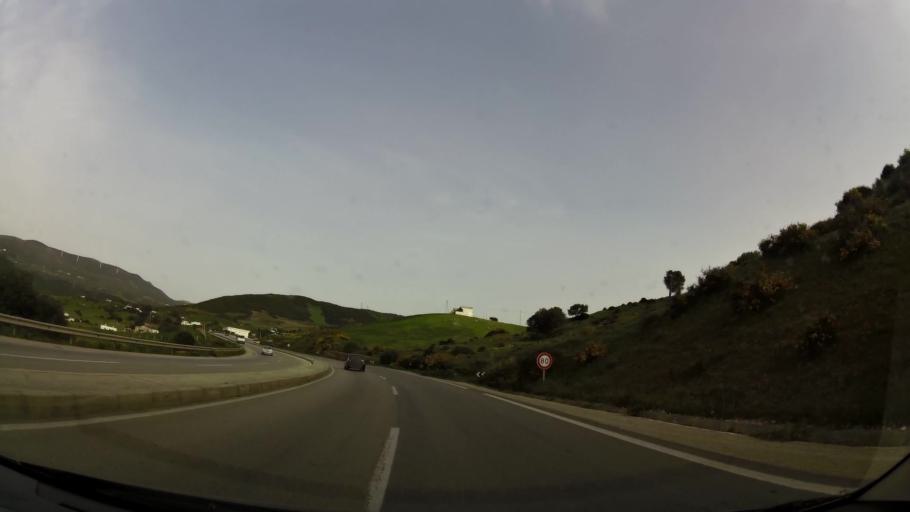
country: MA
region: Tanger-Tetouan
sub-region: Tanger-Assilah
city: Dar Chaoui
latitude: 35.5638
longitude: -5.6047
